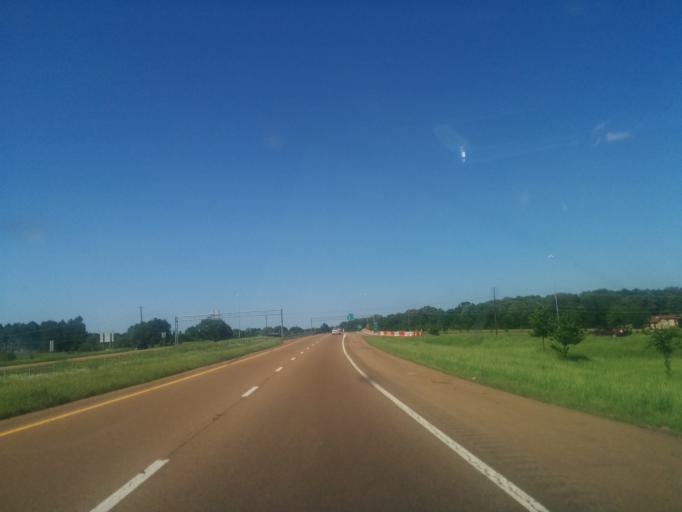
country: US
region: Mississippi
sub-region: Hinds County
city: Jackson
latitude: 32.2985
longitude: -90.2473
